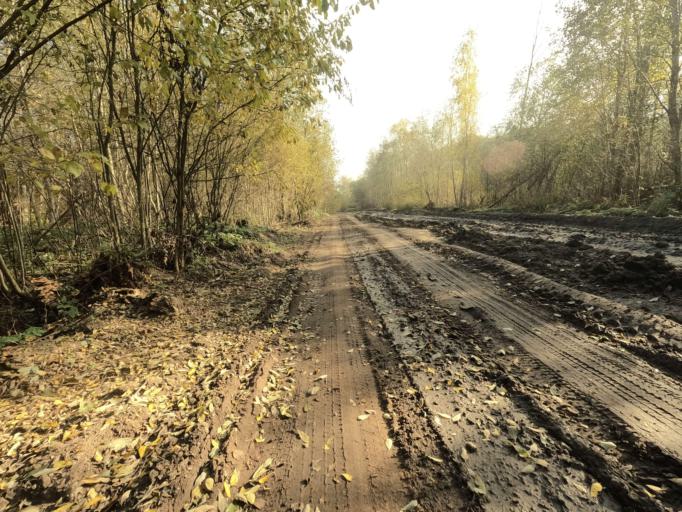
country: RU
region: Novgorod
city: Batetskiy
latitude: 58.8799
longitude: 30.7332
